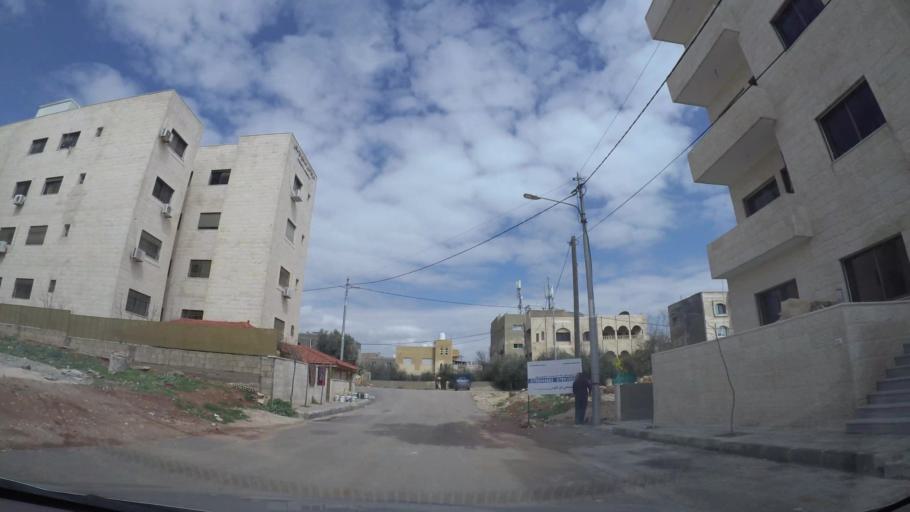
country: JO
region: Amman
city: Al Jubayhah
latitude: 32.0599
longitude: 35.8148
